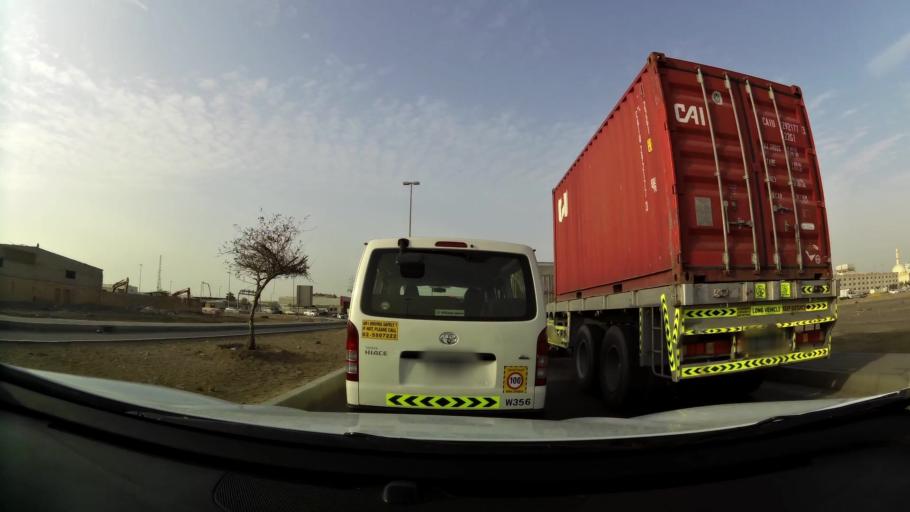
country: AE
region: Abu Dhabi
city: Abu Dhabi
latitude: 24.3586
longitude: 54.5166
